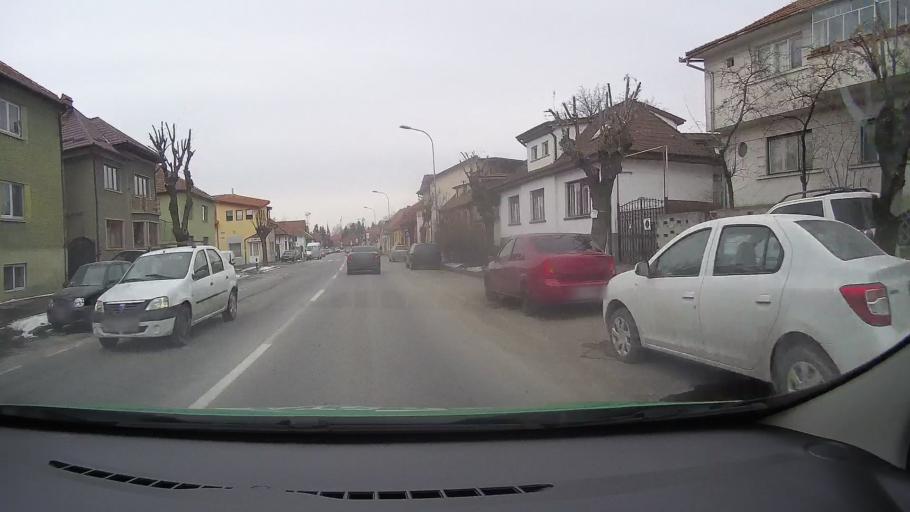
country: RO
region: Brasov
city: Brasov
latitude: 45.6597
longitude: 25.5920
